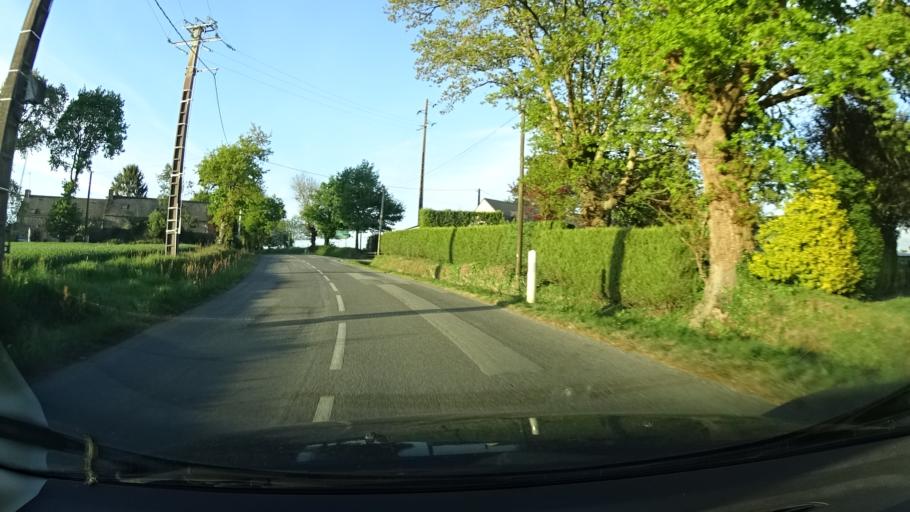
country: FR
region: Brittany
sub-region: Departement du Morbihan
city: Caden
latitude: 47.5918
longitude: -2.2932
